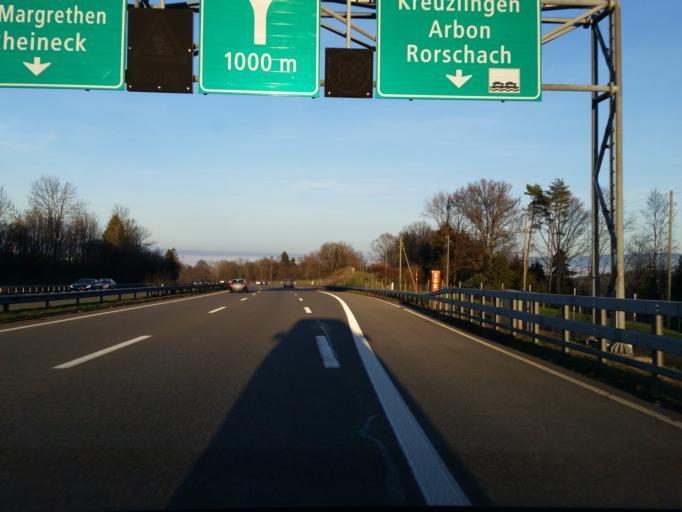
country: CH
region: Saint Gallen
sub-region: Wahlkreis Rorschach
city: Morschwil
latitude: 47.4566
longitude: 9.4320
